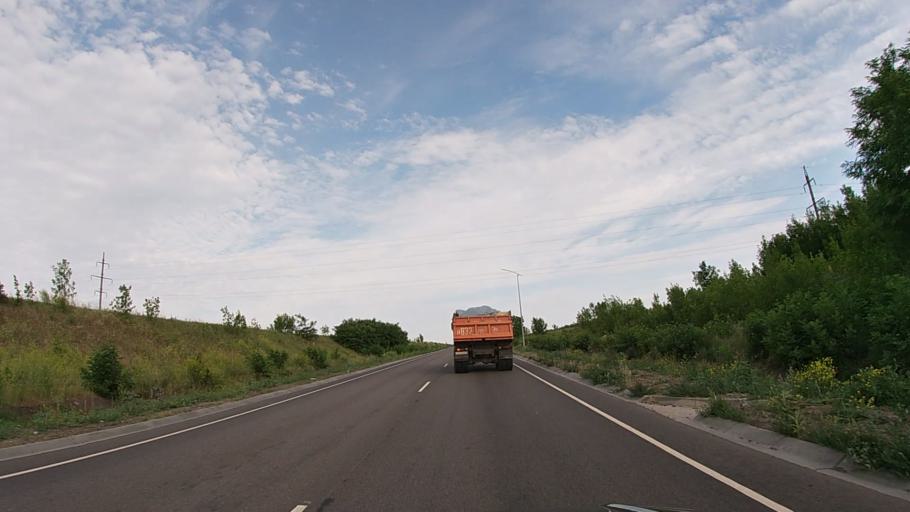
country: RU
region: Belgorod
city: Severnyy
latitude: 50.6700
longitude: 36.4859
